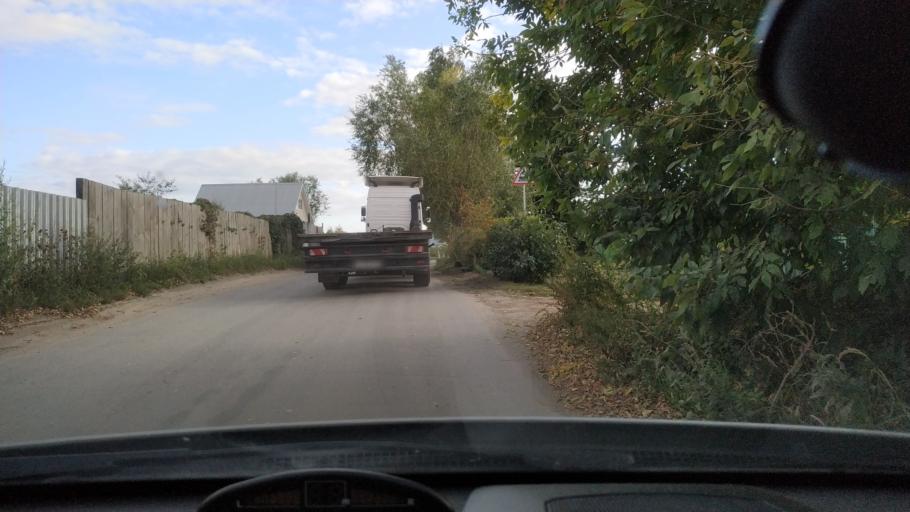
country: RU
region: Rjazan
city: Polyany
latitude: 54.5808
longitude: 39.8389
